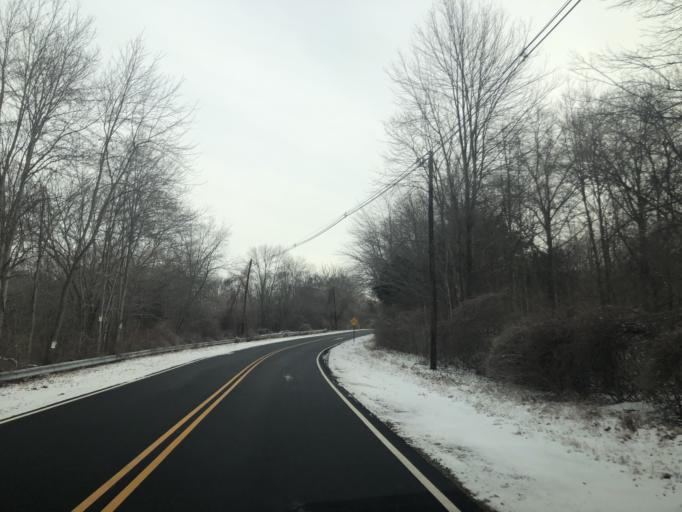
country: US
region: New Jersey
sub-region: Warren County
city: Belvidere
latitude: 40.9313
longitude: -75.0341
